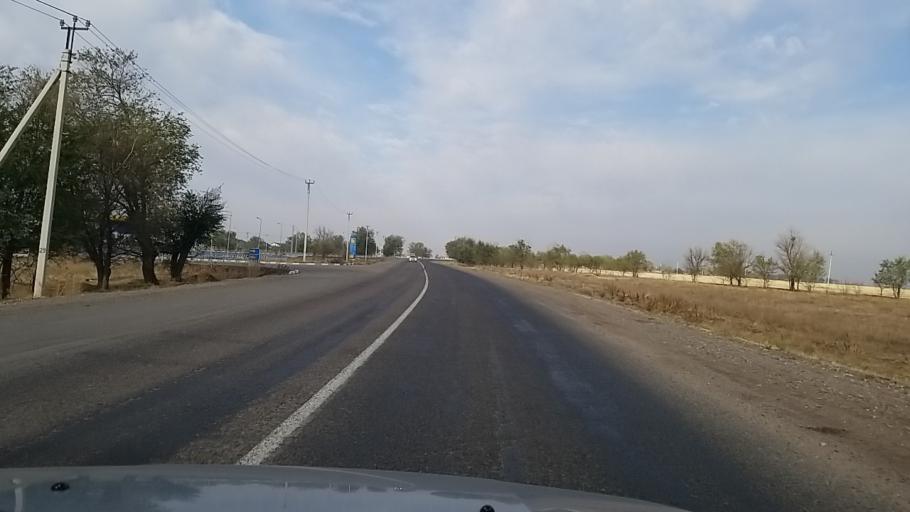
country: KZ
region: Almaty Oblysy
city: Burunday
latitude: 43.4771
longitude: 76.6849
